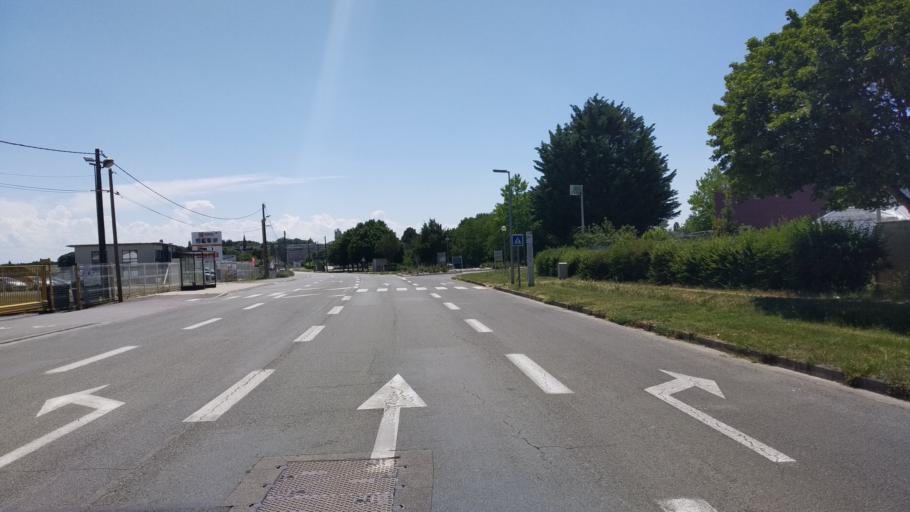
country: FR
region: Poitou-Charentes
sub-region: Departement de la Vienne
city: Biard
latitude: 46.6019
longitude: 0.3054
